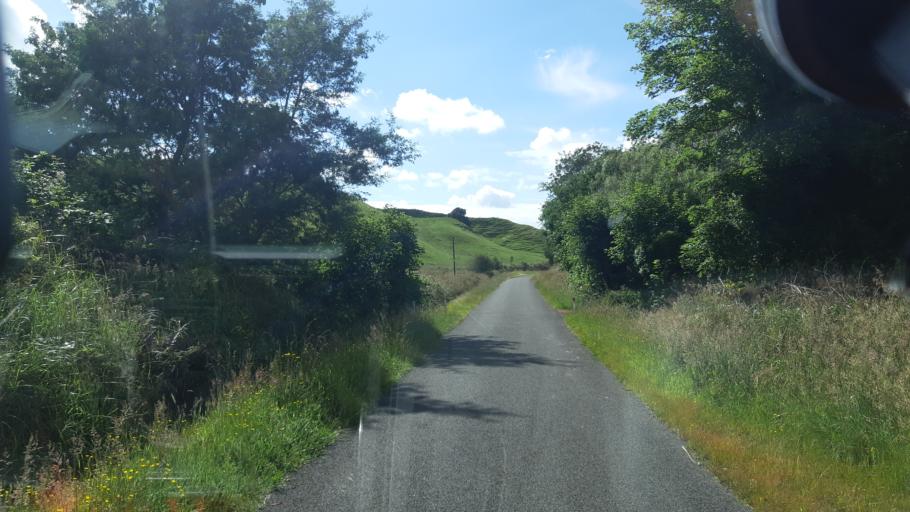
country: NZ
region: Manawatu-Wanganui
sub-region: Rangitikei District
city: Bulls
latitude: -39.9622
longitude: 175.5141
